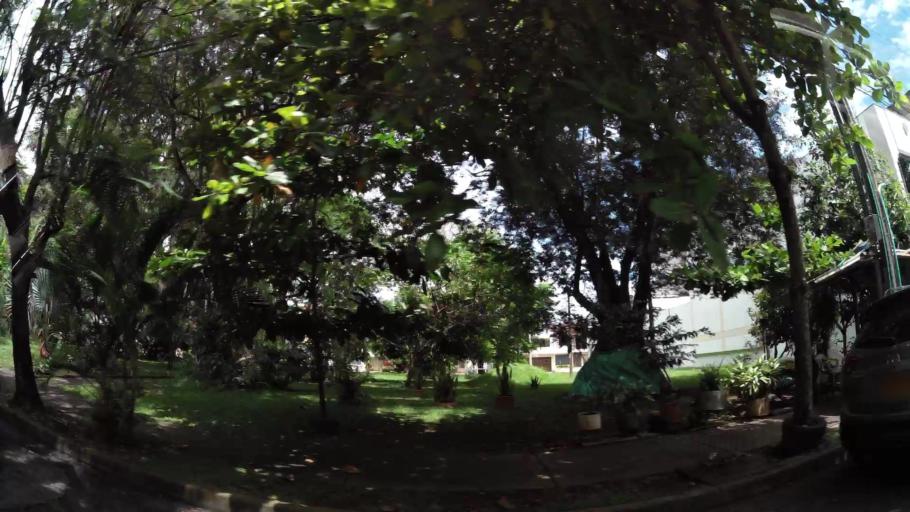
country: CO
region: Valle del Cauca
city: Cali
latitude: 3.3842
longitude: -76.5314
